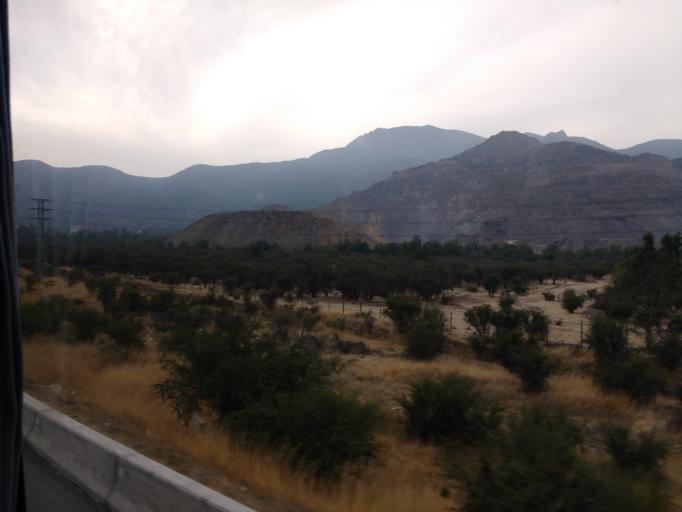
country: CL
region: Santiago Metropolitan
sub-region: Provincia de Talagante
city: Penaflor
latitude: -33.4577
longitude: -70.9151
